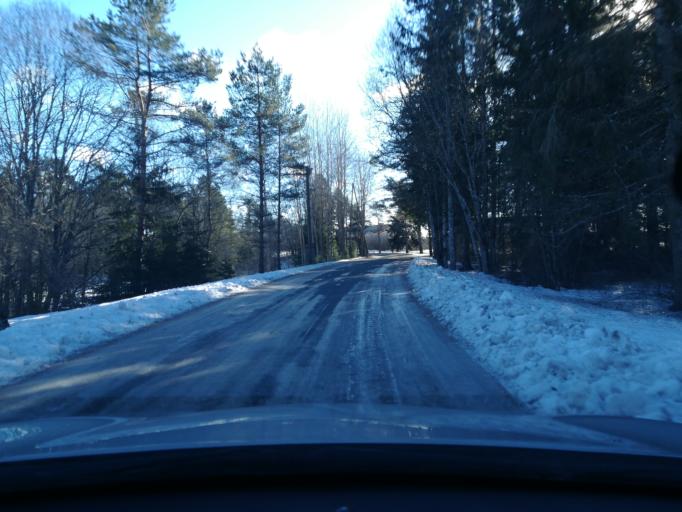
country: EE
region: Raplamaa
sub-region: Kohila vald
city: Kohila
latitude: 59.2290
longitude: 24.7512
